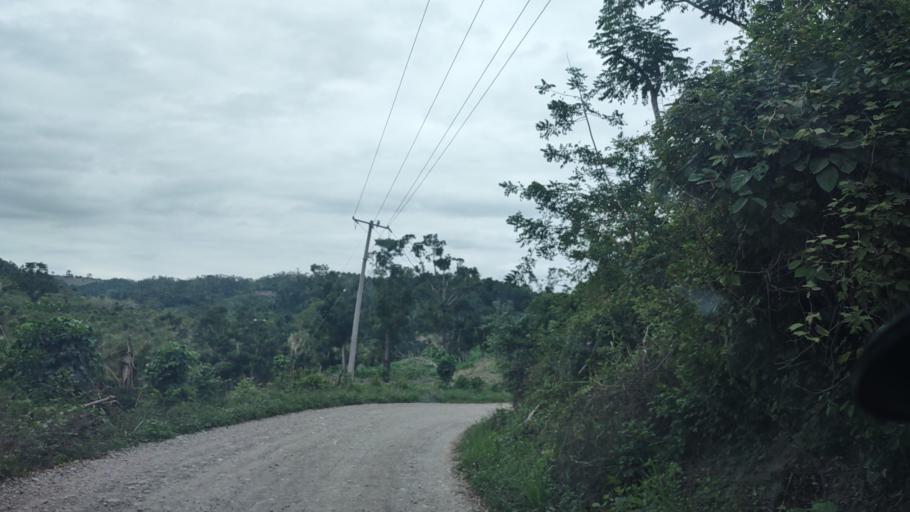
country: MX
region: Veracruz
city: Papantla de Olarte
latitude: 20.4371
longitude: -97.2748
